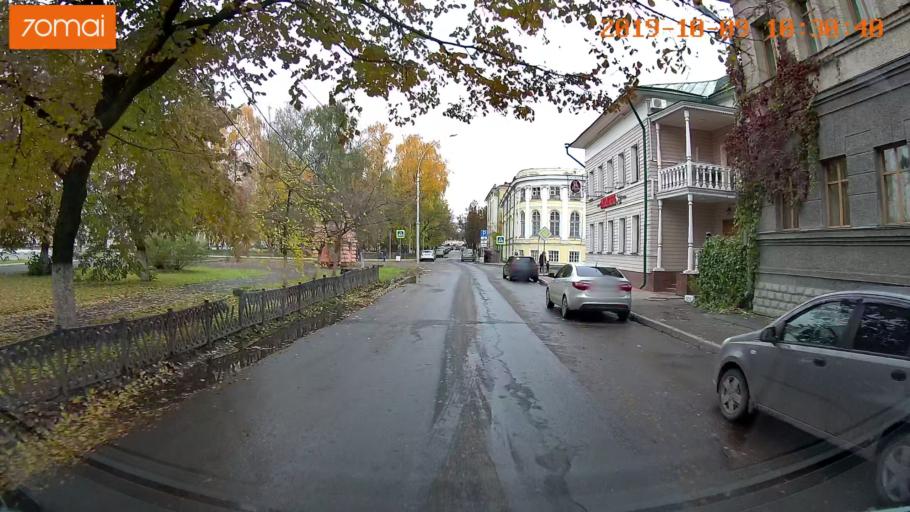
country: RU
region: Vologda
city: Vologda
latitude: 59.2191
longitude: 39.8951
